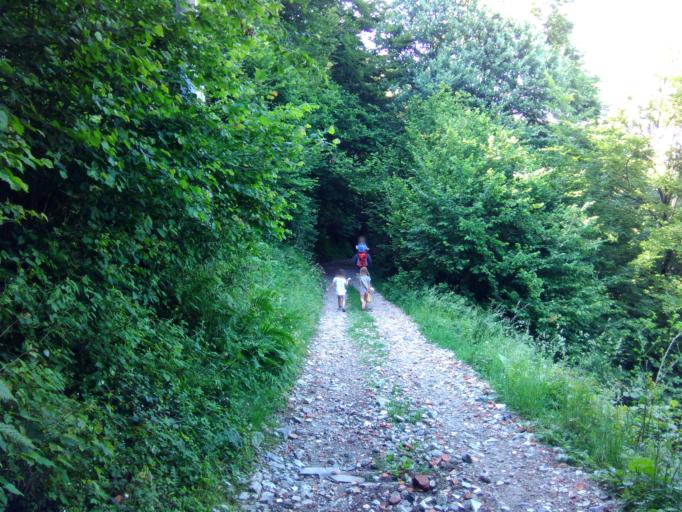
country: IT
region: Lombardy
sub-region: Provincia di Como
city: Casasco Intelvi
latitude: 45.9402
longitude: 9.0656
